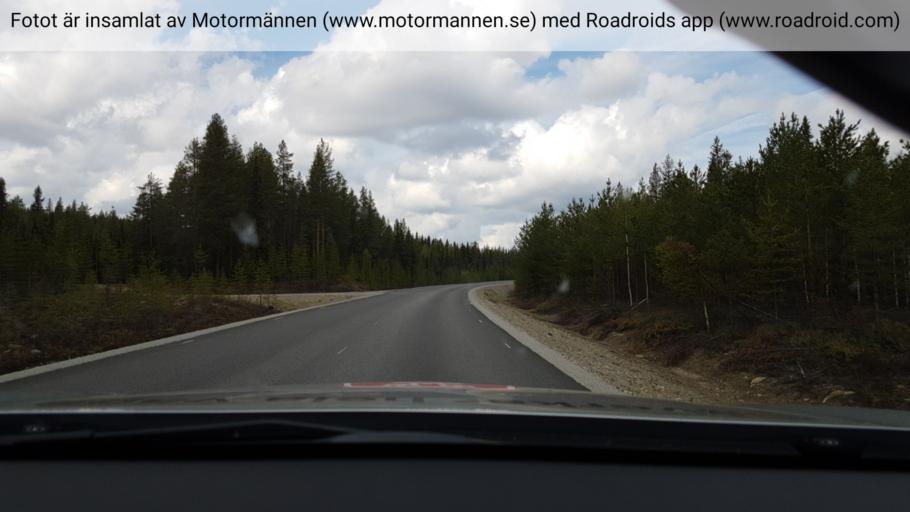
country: SE
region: Vaesterbotten
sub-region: Lycksele Kommun
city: Lycksele
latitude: 64.0189
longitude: 18.4524
